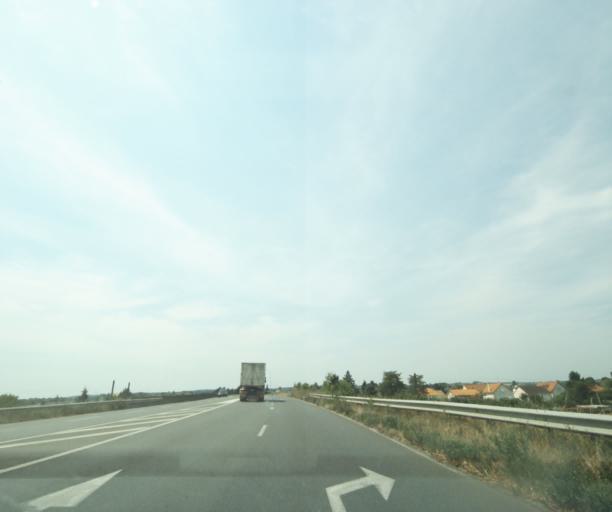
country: FR
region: Poitou-Charentes
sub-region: Departement de la Vienne
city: Antran
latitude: 46.8376
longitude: 0.5508
